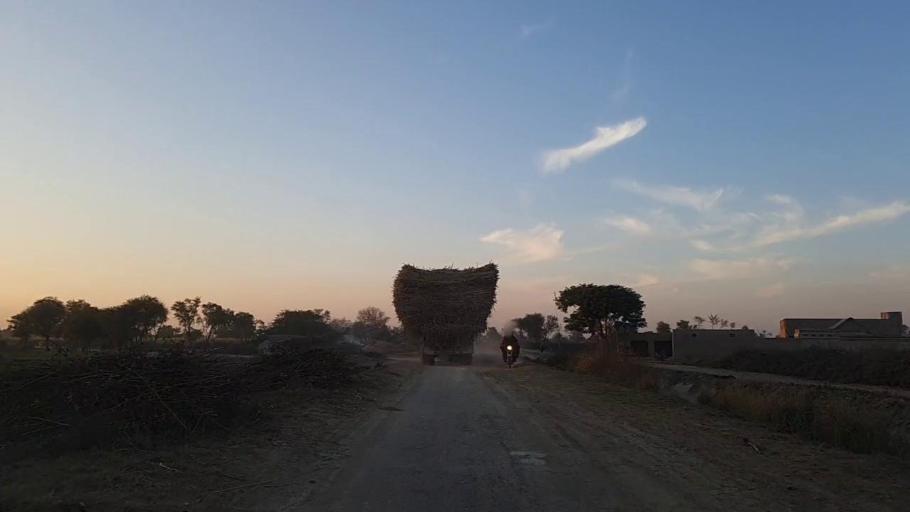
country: PK
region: Sindh
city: Bandhi
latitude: 26.6211
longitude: 68.3487
